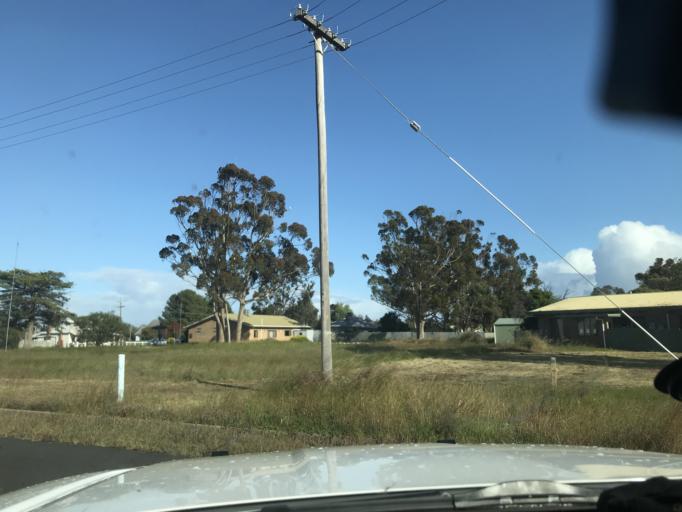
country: AU
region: Victoria
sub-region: Horsham
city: Horsham
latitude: -36.7200
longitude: 141.4767
